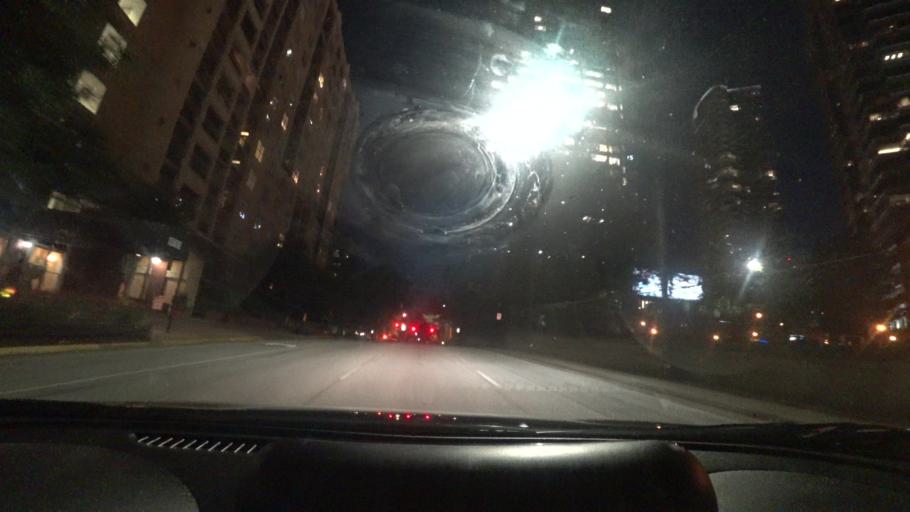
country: US
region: Georgia
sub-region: Fulton County
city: Atlanta
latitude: 33.7852
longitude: -84.3824
